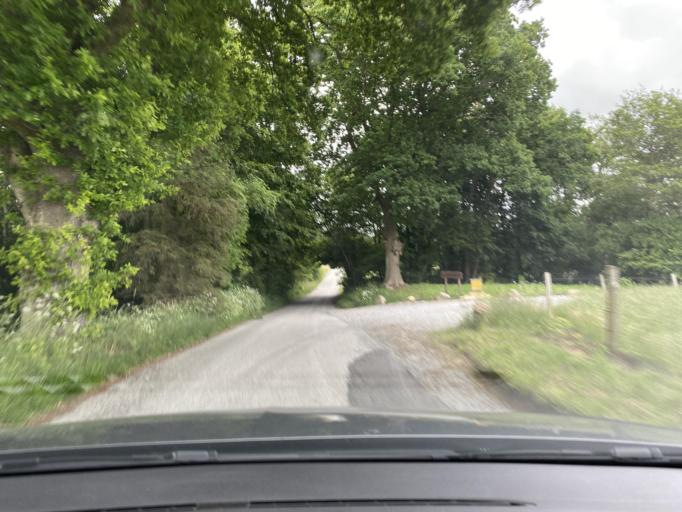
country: DK
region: South Denmark
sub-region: Vejle Kommune
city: Brejning
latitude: 55.6369
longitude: 9.7325
